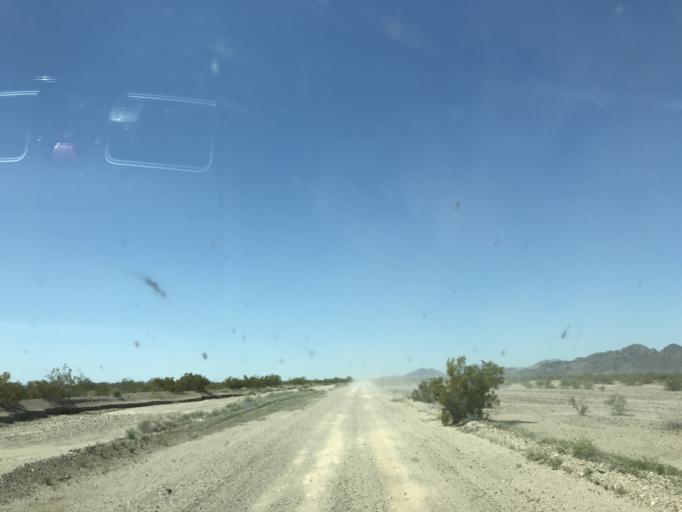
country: US
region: California
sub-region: Riverside County
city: Mesa Verde
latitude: 33.4882
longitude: -114.8996
